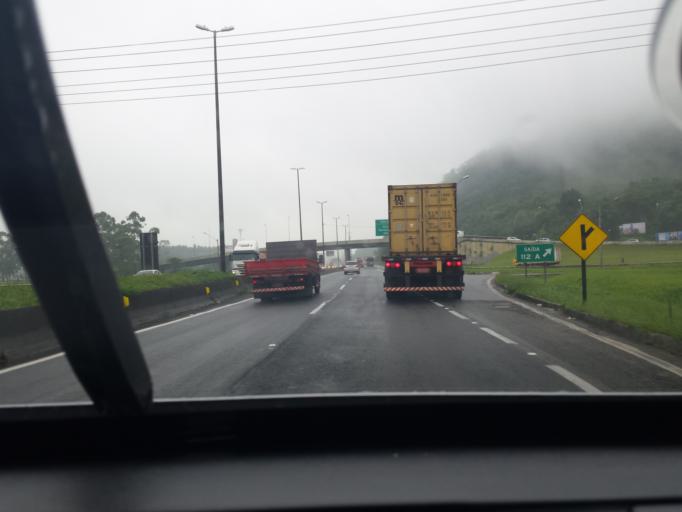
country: BR
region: Santa Catarina
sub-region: Navegantes
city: Navegantes
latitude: -26.8429
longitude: -48.7176
